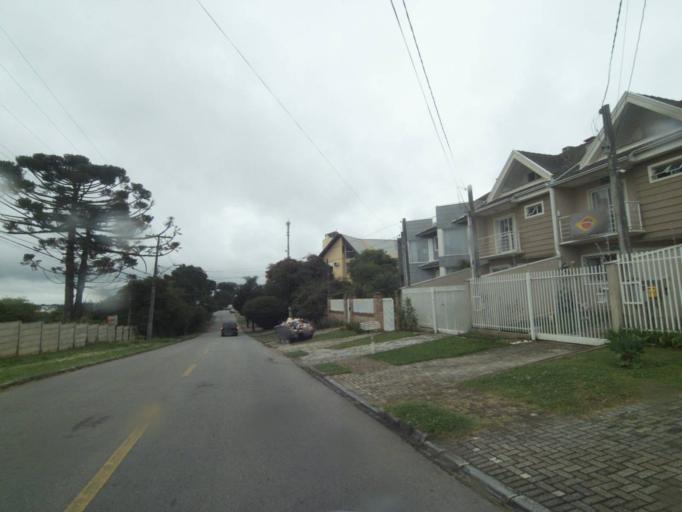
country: BR
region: Parana
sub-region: Curitiba
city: Curitiba
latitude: -25.4216
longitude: -49.3335
